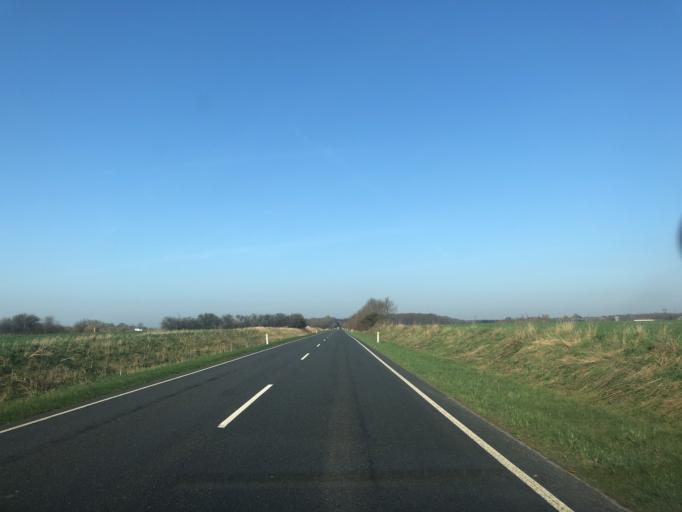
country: DK
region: Zealand
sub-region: Faxe Kommune
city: Fakse Ladeplads
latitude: 55.2798
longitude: 12.1951
